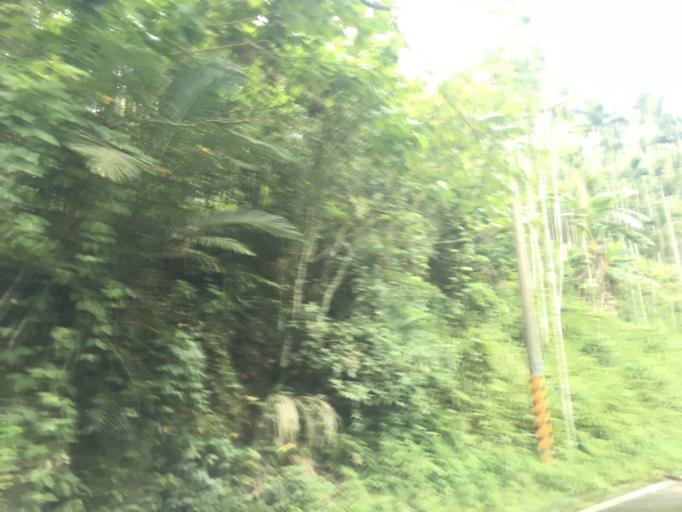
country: TW
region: Taiwan
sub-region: Yunlin
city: Douliu
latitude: 23.5676
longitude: 120.6474
